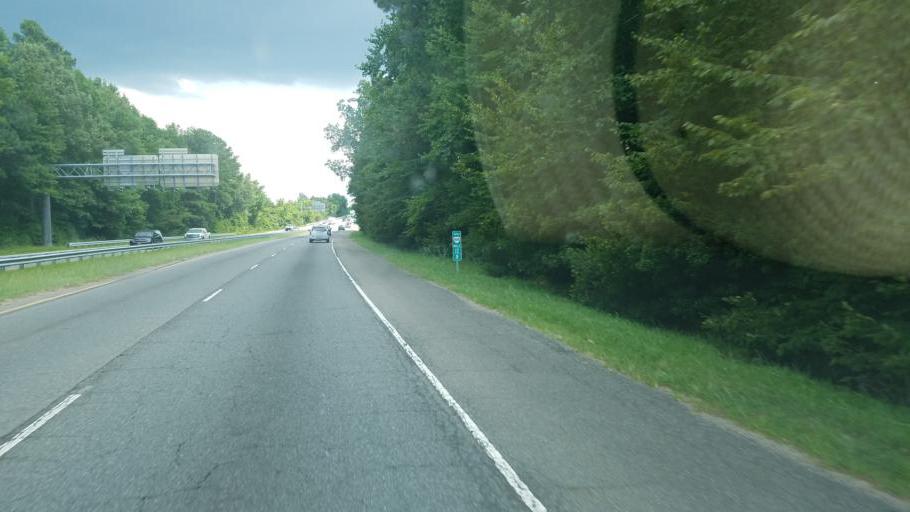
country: US
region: Virginia
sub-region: City of Chesapeake
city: Chesapeake
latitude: 36.7284
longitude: -76.2305
